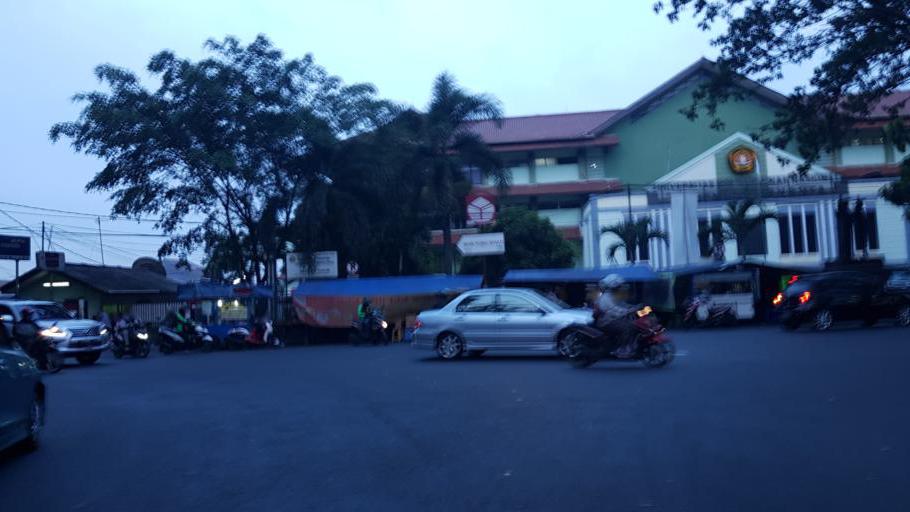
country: ID
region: West Java
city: Pamulang
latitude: -6.3156
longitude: 106.7928
